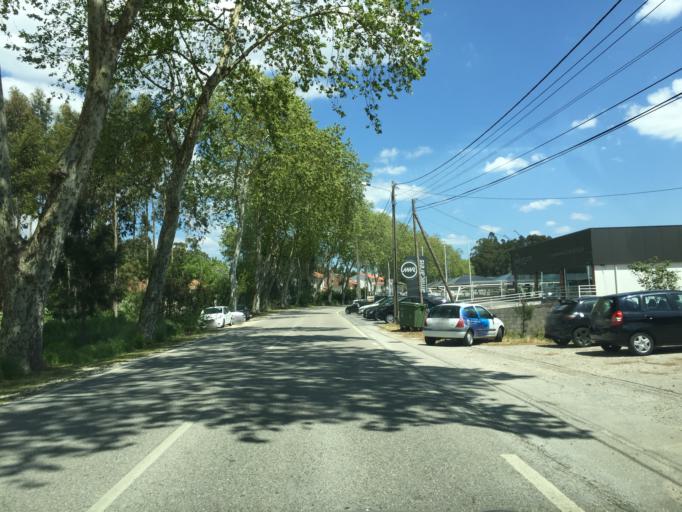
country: PT
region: Leiria
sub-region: Leiria
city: Santa Catarina da Serra
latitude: 39.6361
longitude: -8.6949
